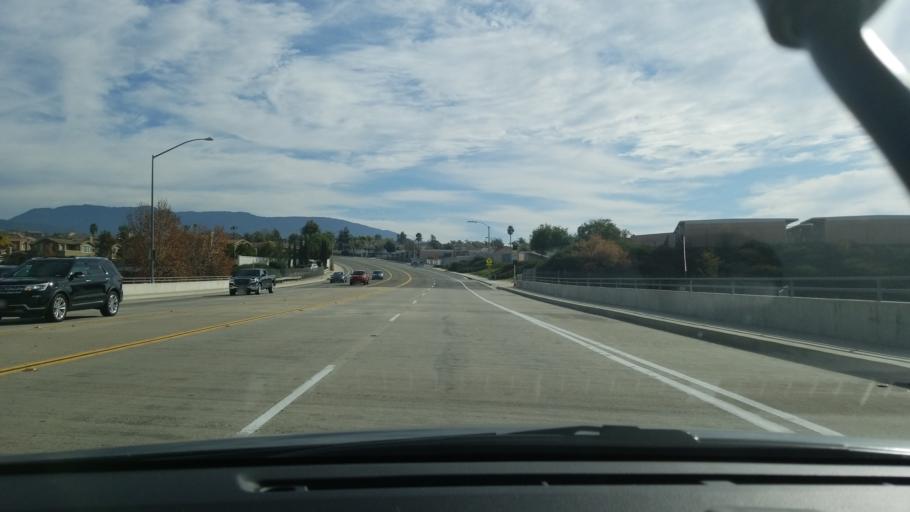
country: US
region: California
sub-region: Riverside County
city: Temecula
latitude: 33.4835
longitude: -117.0771
